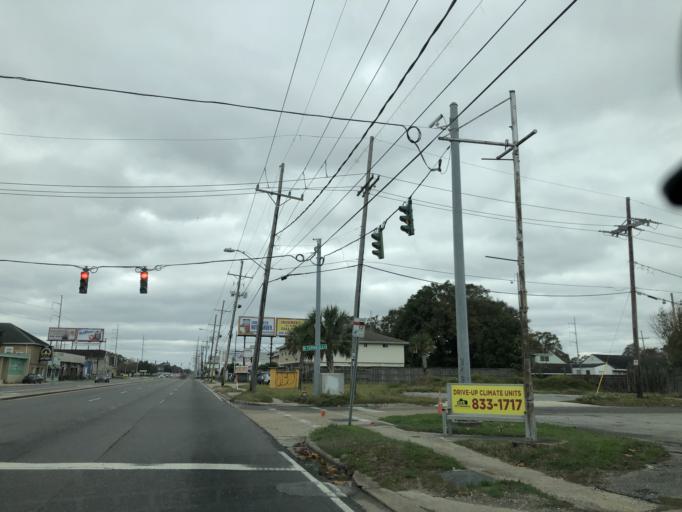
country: US
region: Louisiana
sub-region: Jefferson Parish
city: Metairie Terrace
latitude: 29.9753
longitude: -90.1669
